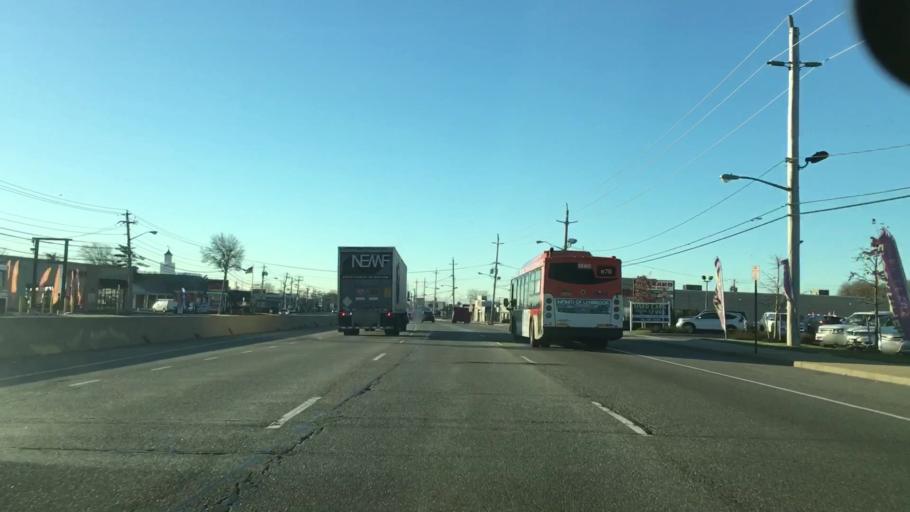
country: US
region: New York
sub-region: Suffolk County
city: East Farmingdale
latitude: 40.7461
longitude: -73.4227
